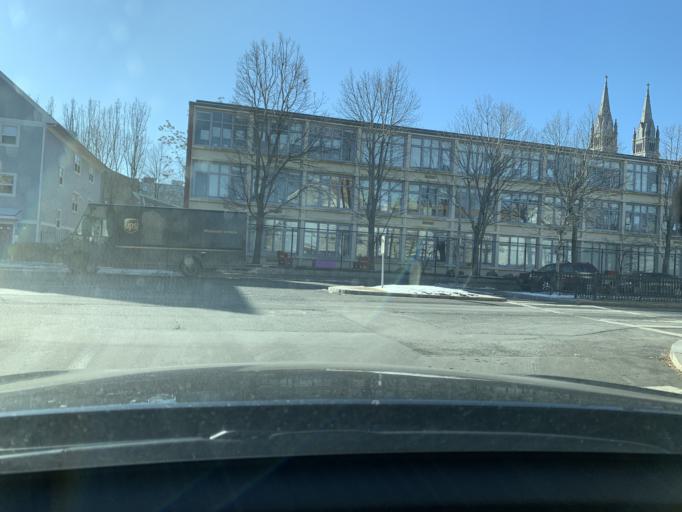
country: US
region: Massachusetts
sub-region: Norfolk County
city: Brookline
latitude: 42.3335
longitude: -71.0977
